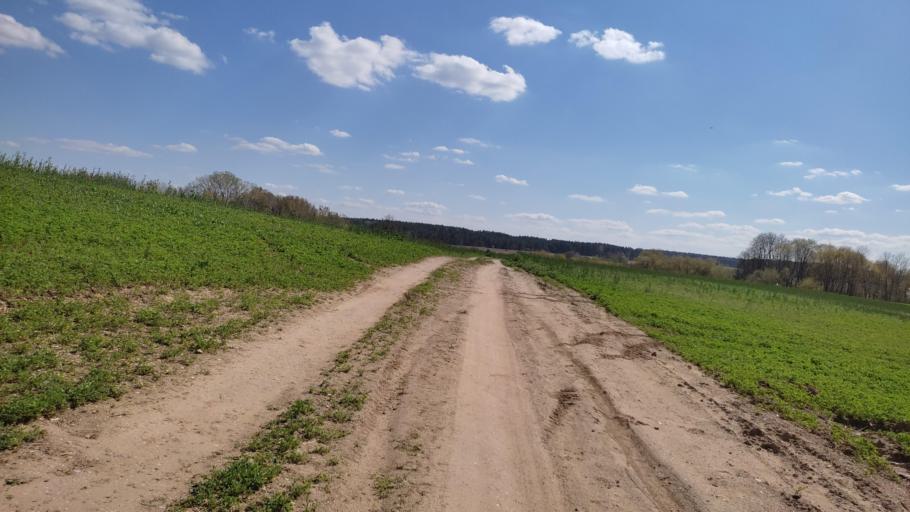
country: BY
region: Grodnenskaya
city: Hrodna
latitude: 53.6566
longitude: 23.9058
